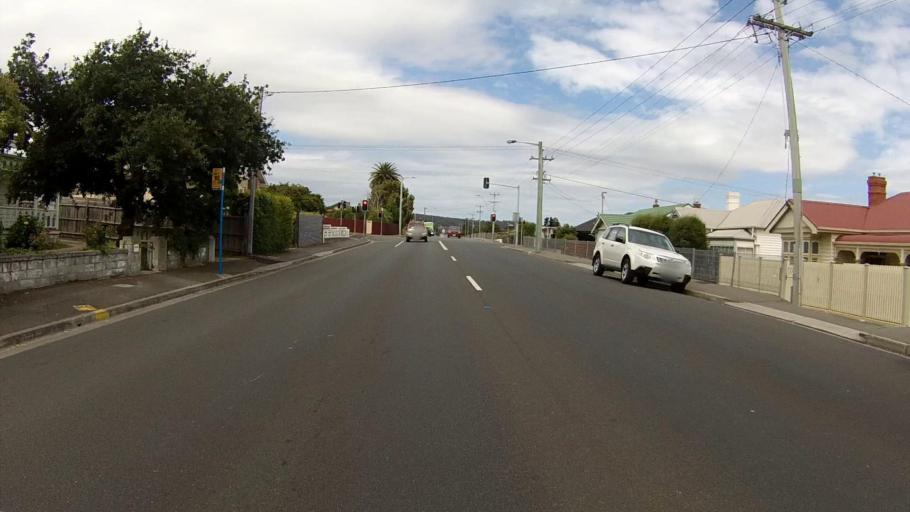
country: AU
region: Tasmania
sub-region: Clarence
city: Bellerive
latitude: -42.8751
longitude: 147.3753
